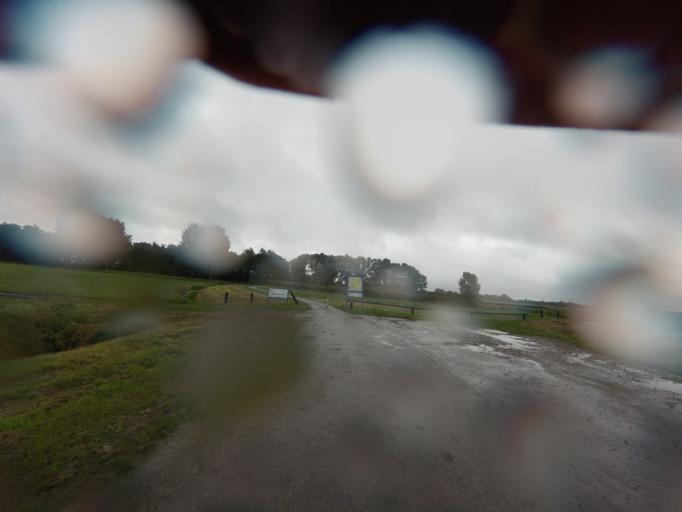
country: NL
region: North Holland
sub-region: Gemeente Medemblik
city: Opperdoes
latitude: 52.7205
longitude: 5.1052
